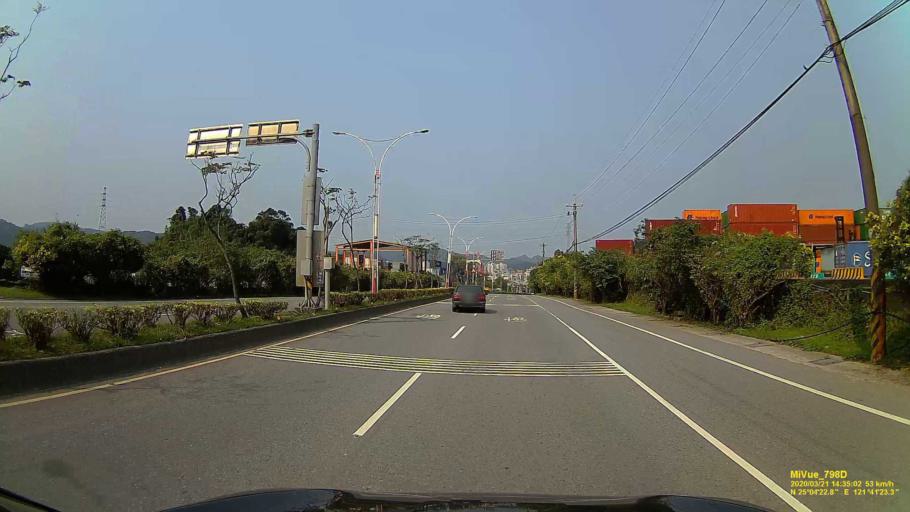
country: TW
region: Taiwan
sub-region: Keelung
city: Keelung
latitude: 25.0732
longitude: 121.6899
